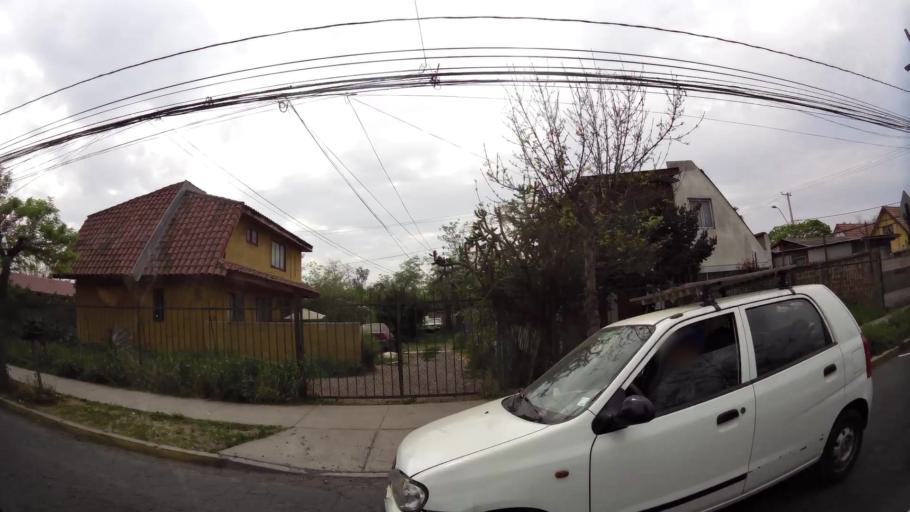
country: CL
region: Santiago Metropolitan
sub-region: Provincia de Santiago
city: Lo Prado
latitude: -33.5092
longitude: -70.7660
